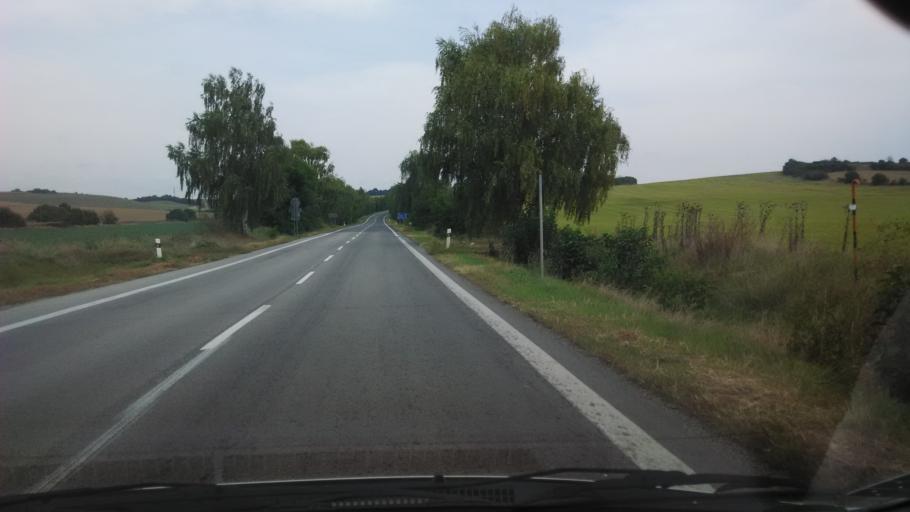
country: SK
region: Nitriansky
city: Zeliezovce
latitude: 48.1256
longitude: 18.7027
